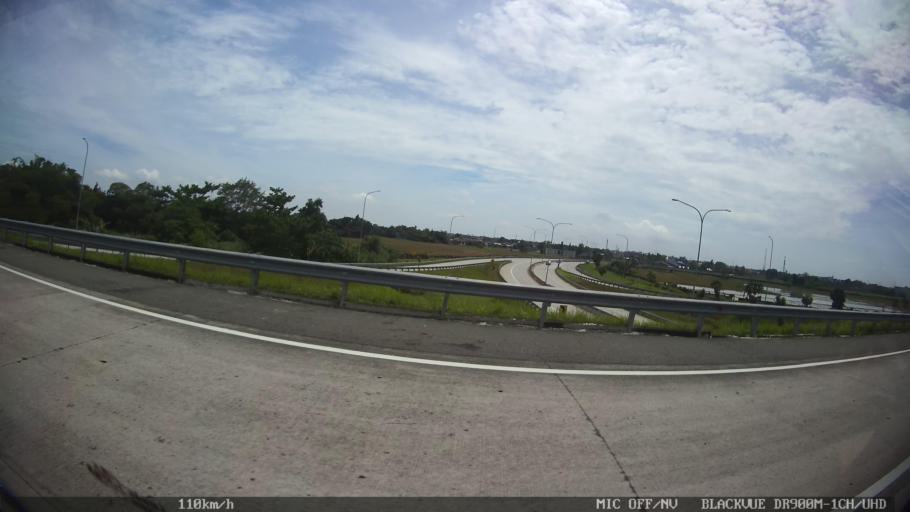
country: ID
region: North Sumatra
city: Percut
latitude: 3.5616
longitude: 98.8507
